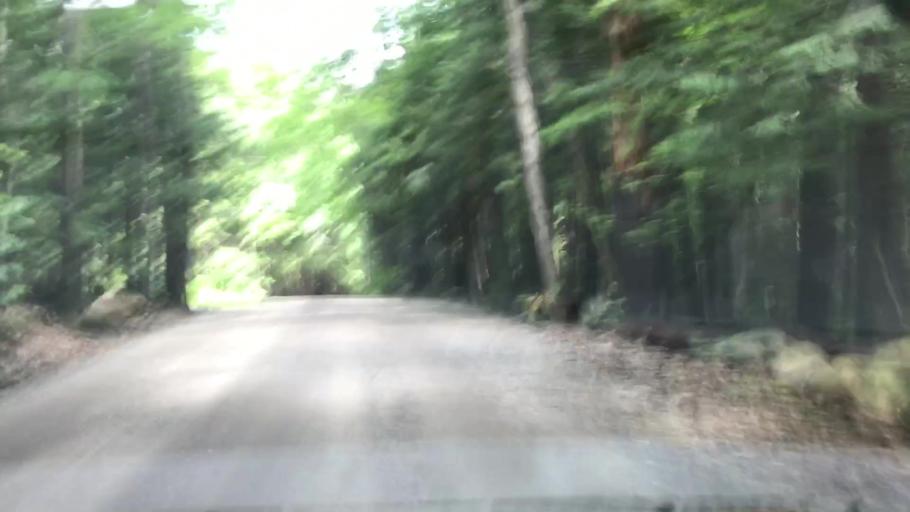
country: US
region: New Hampshire
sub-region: Hillsborough County
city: Milford
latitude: 42.8810
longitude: -71.6163
